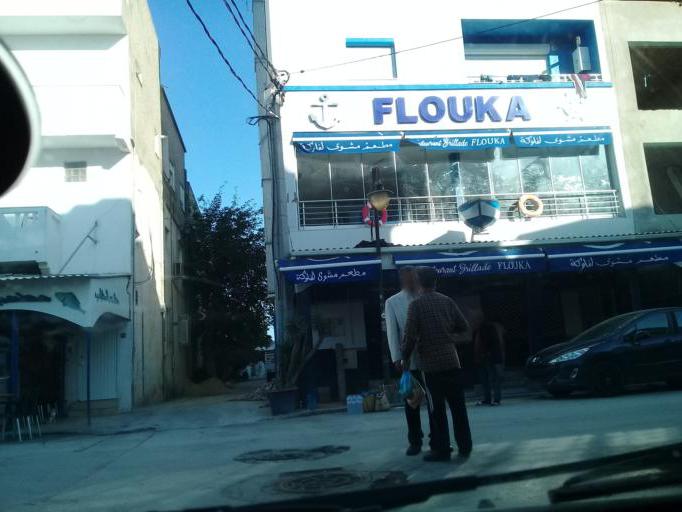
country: TN
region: Tunis
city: La Goulette
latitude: 36.8188
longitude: 10.3071
